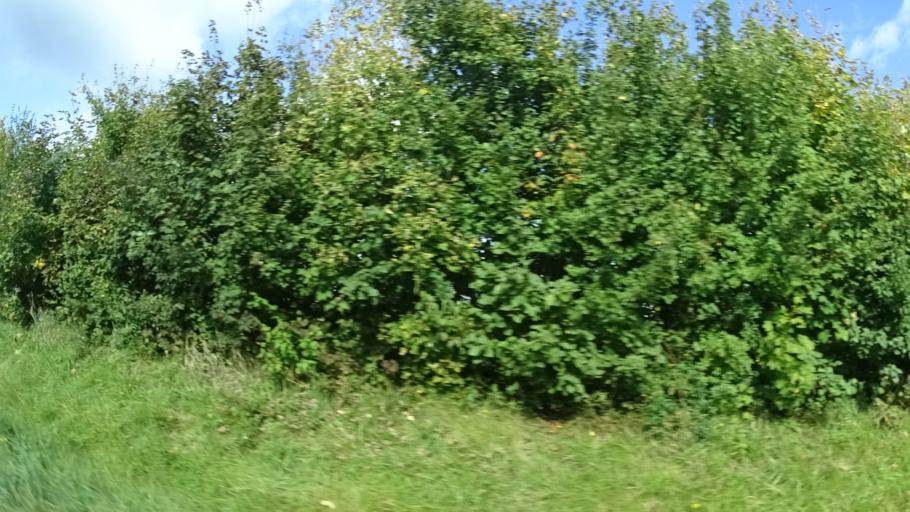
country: DE
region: Bavaria
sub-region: Regierungsbezirk Unterfranken
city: Frickenhausen
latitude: 49.7091
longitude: 10.0713
